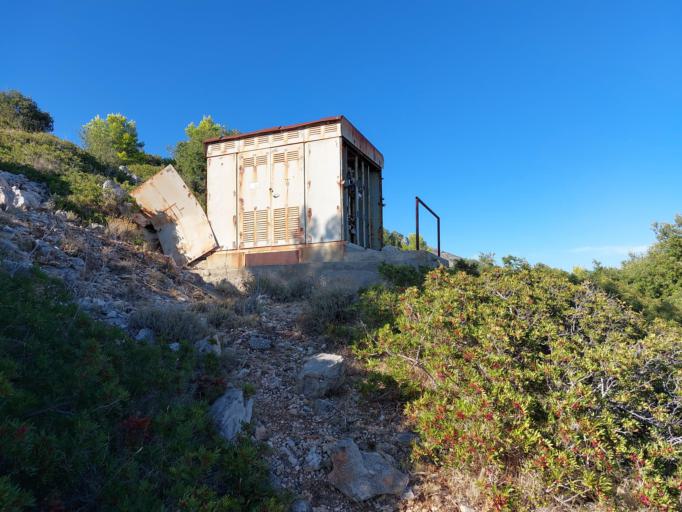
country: HR
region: Dubrovacko-Neretvanska
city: Smokvica
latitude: 42.7275
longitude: 16.8416
